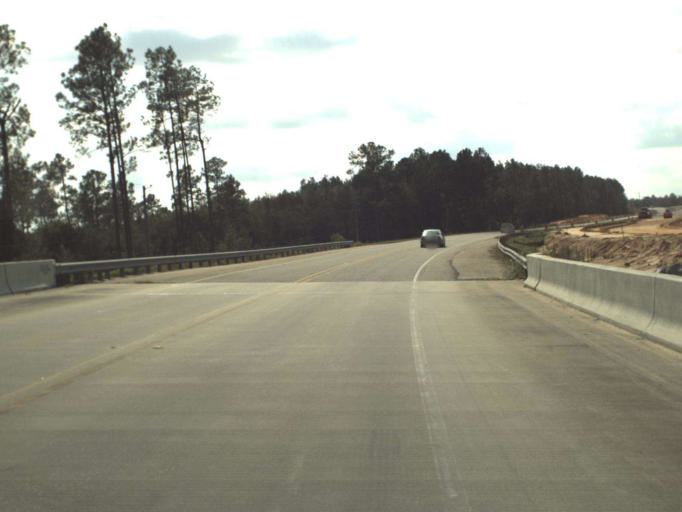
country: US
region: Florida
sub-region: Holmes County
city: Bonifay
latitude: 30.6679
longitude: -85.6884
